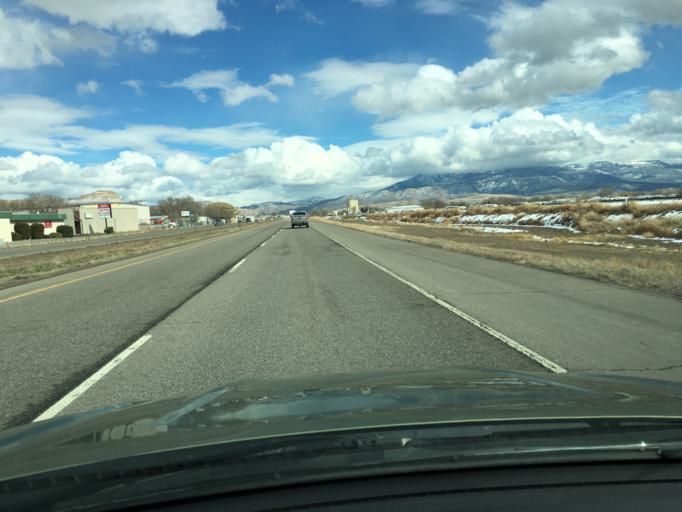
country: US
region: Colorado
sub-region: Mesa County
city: Fruitvale
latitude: 39.0742
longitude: -108.5089
